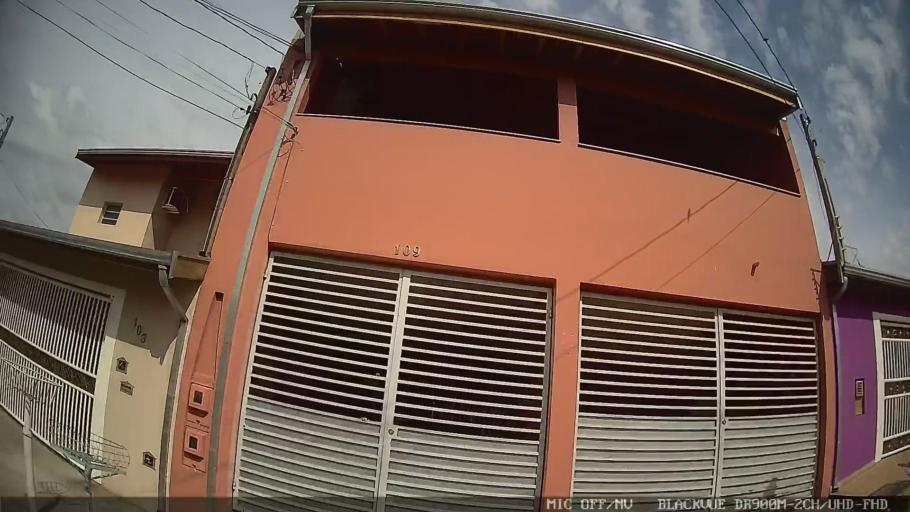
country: BR
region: Sao Paulo
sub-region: Indaiatuba
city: Indaiatuba
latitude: -23.1246
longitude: -47.2493
